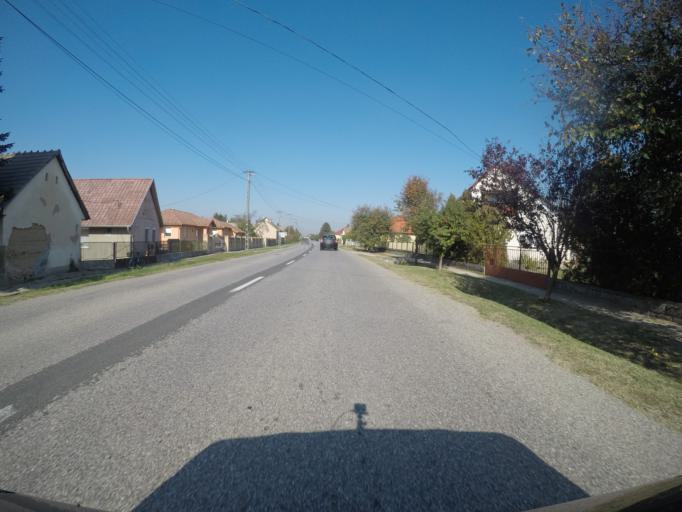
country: HU
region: Tolna
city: Szedres
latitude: 46.4772
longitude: 18.6837
